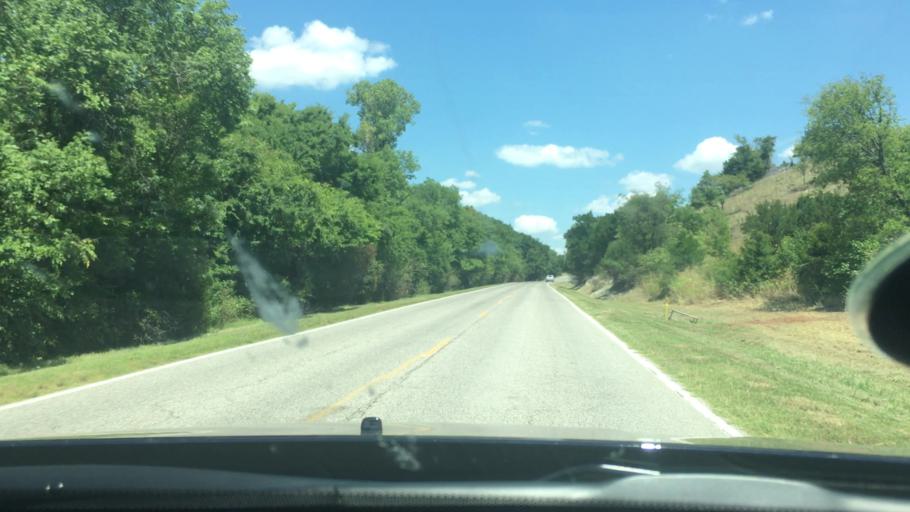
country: US
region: Oklahoma
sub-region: Carter County
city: Dickson
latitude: 34.3119
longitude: -96.9624
